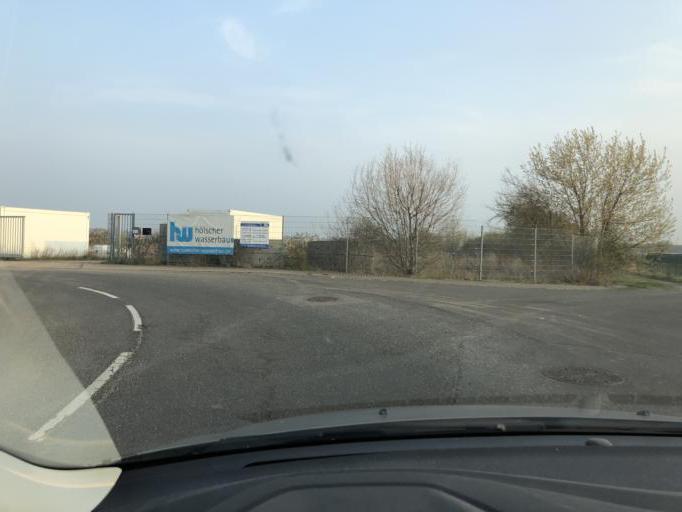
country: DE
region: Saxony
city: Rackwitz
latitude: 51.4031
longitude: 12.3577
